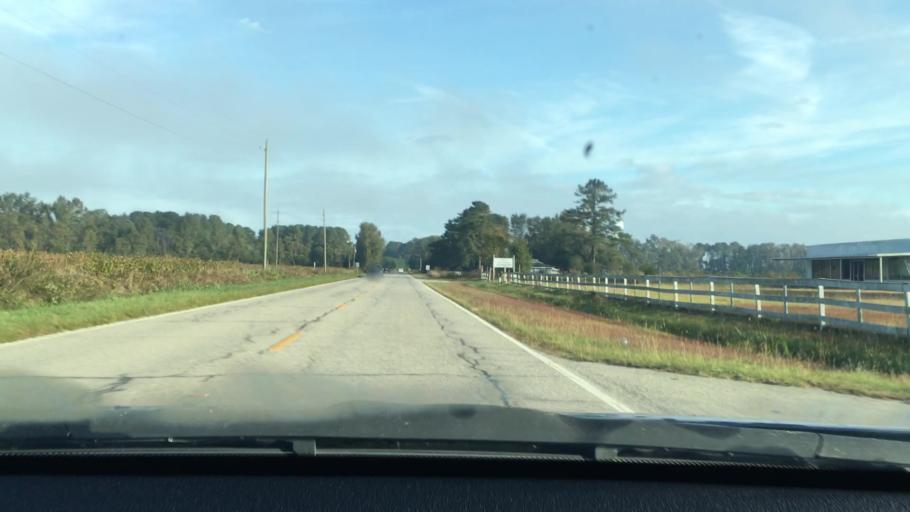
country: US
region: South Carolina
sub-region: Sumter County
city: East Sumter
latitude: 34.0020
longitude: -80.2882
